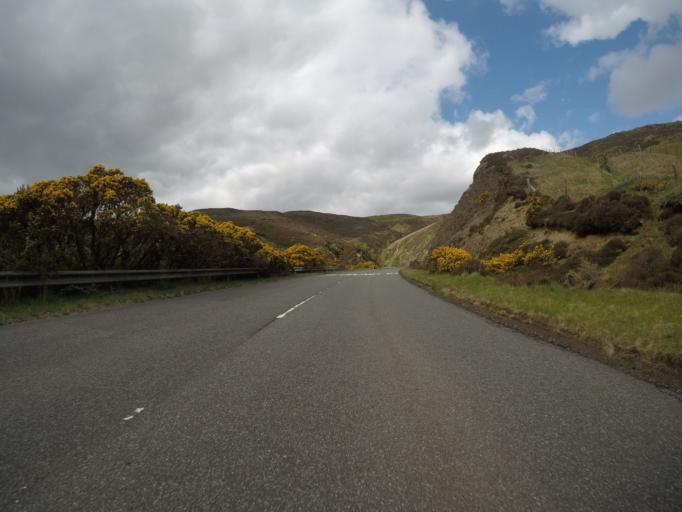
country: GB
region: Scotland
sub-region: Highland
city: Isle of Skye
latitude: 57.3054
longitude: -6.3075
